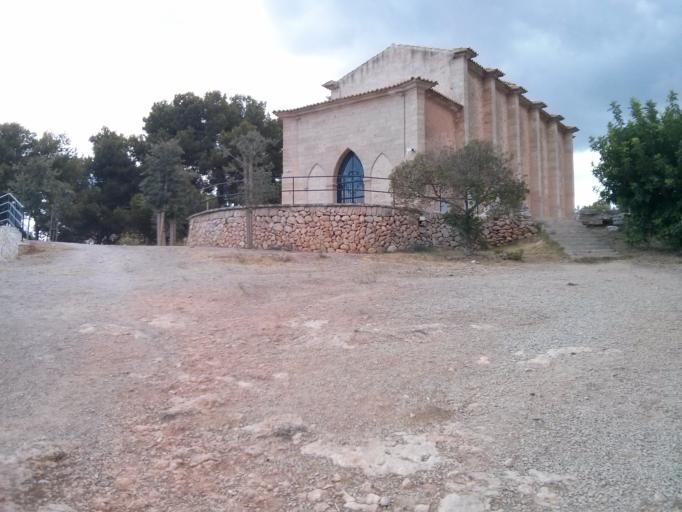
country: ES
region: Balearic Islands
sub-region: Illes Balears
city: Magaluf
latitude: 39.5324
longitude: 2.5744
